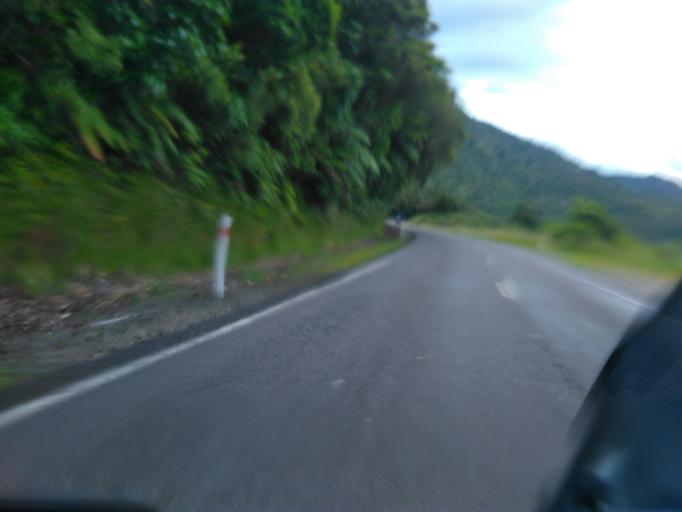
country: NZ
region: Bay of Plenty
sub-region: Opotiki District
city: Opotiki
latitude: -38.2289
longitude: 177.3098
